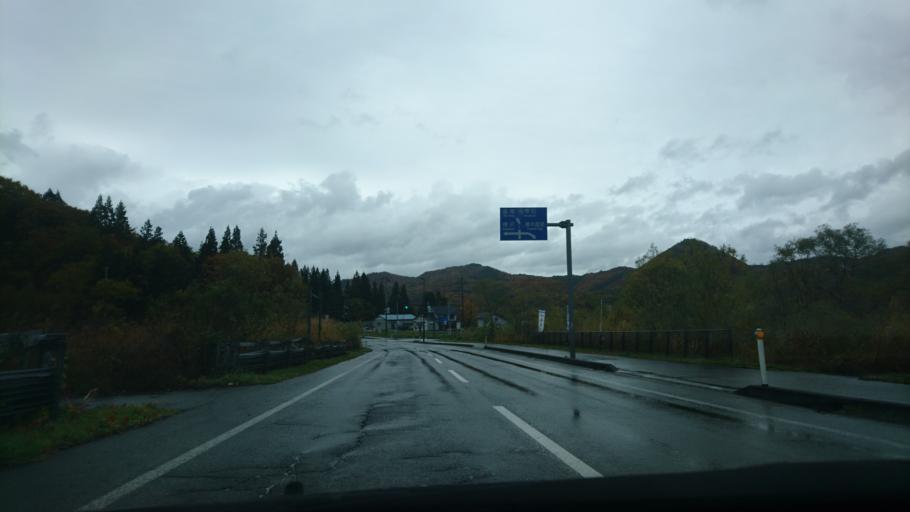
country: JP
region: Akita
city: Yokotemachi
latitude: 39.3597
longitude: 140.7620
